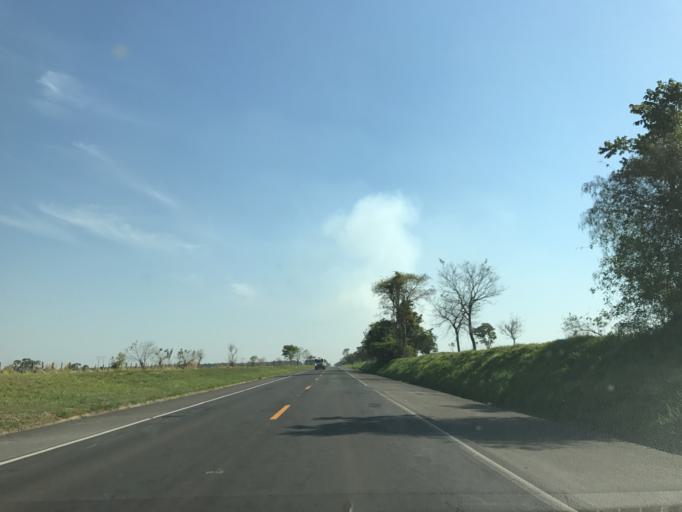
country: BR
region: Sao Paulo
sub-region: Penapolis
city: Penapolis
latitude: -21.3631
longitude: -50.0707
